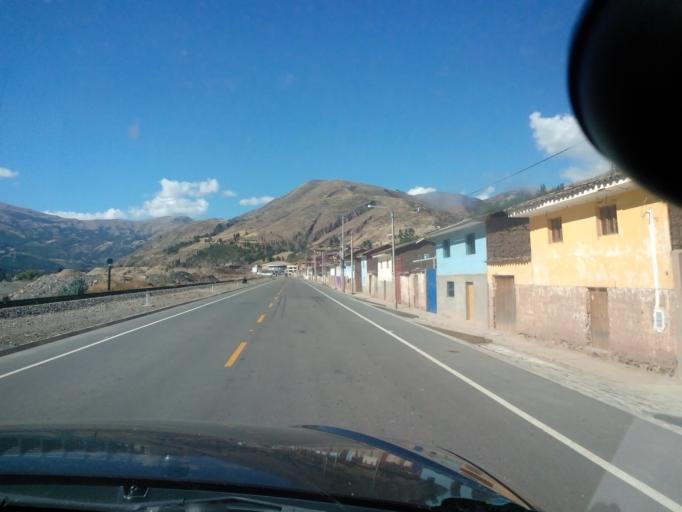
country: PE
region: Cusco
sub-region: Provincia de Quispicanchis
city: Urcos
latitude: -13.6785
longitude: -71.6279
